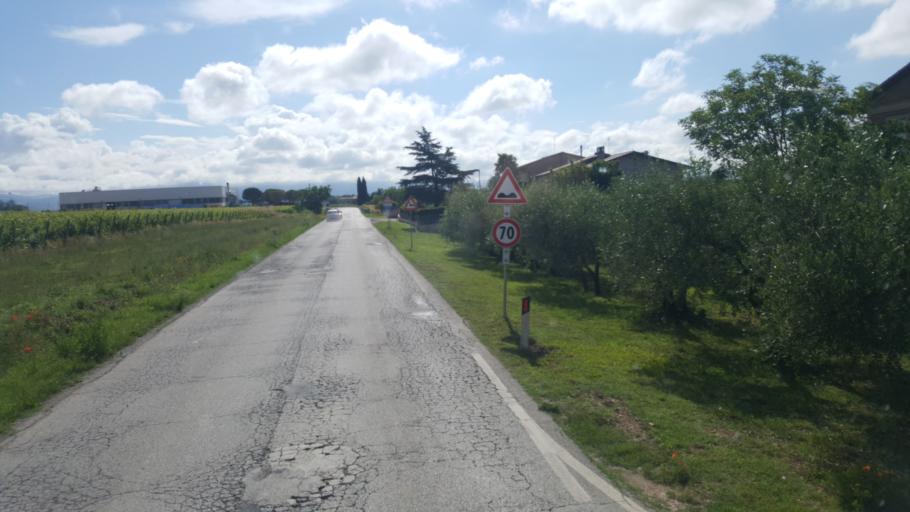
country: IT
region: Umbria
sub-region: Provincia di Perugia
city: Torgiano
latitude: 43.0392
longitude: 12.4695
